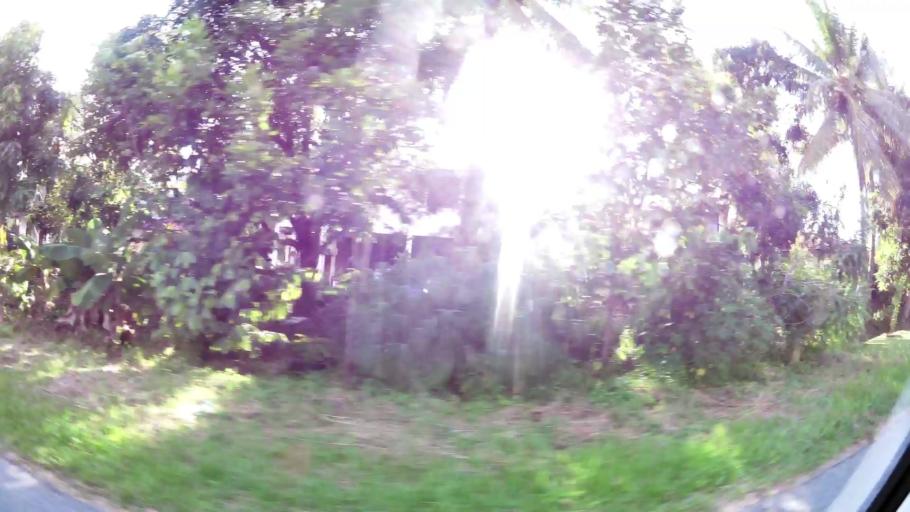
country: BN
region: Brunei and Muara
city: Bandar Seri Begawan
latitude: 4.9844
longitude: 114.9685
